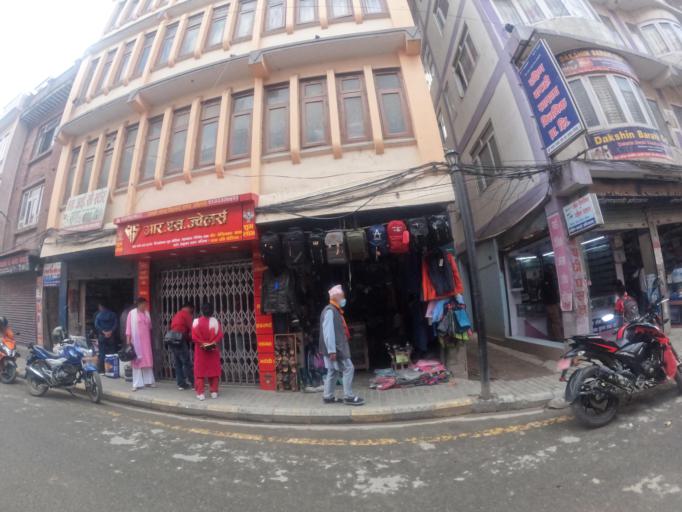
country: NP
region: Central Region
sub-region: Bagmati Zone
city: Bhaktapur
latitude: 27.6719
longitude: 85.3856
